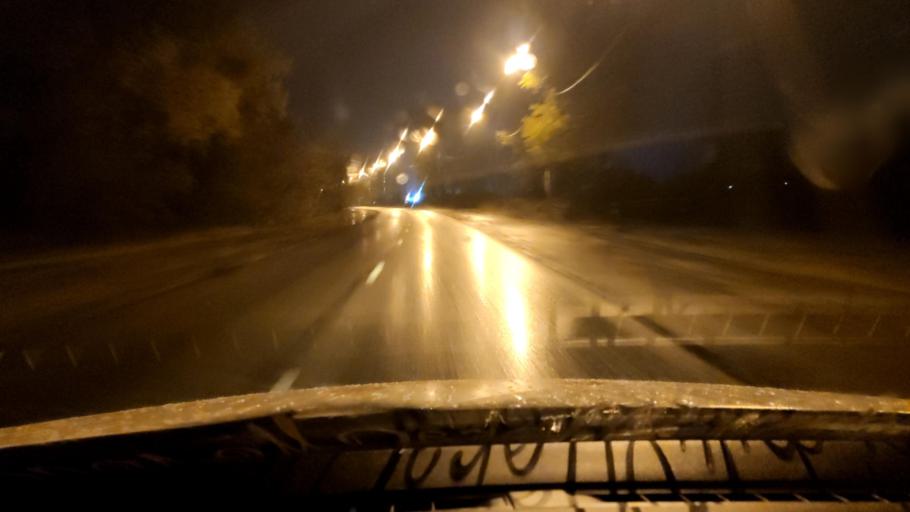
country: RU
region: Voronezj
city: Pridonskoy
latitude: 51.6915
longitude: 39.0831
